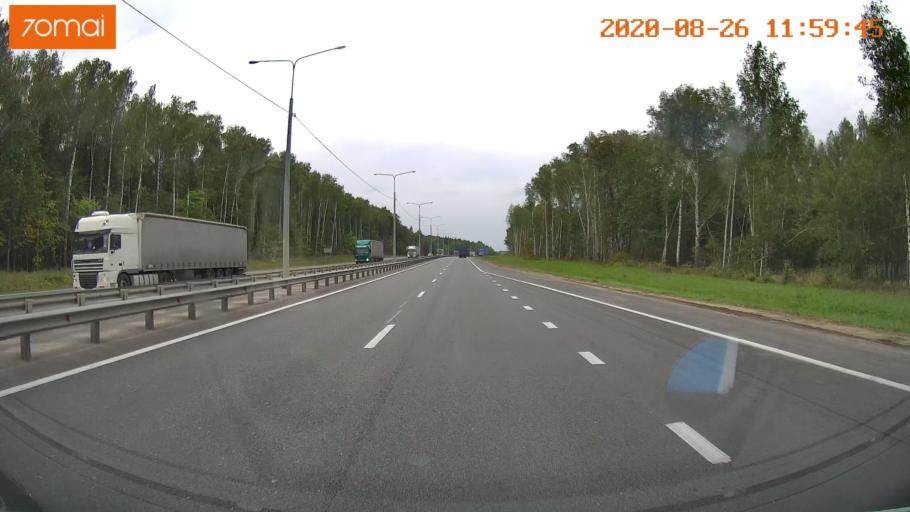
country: RU
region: Rjazan
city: Kiritsy
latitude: 54.2860
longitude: 40.2917
